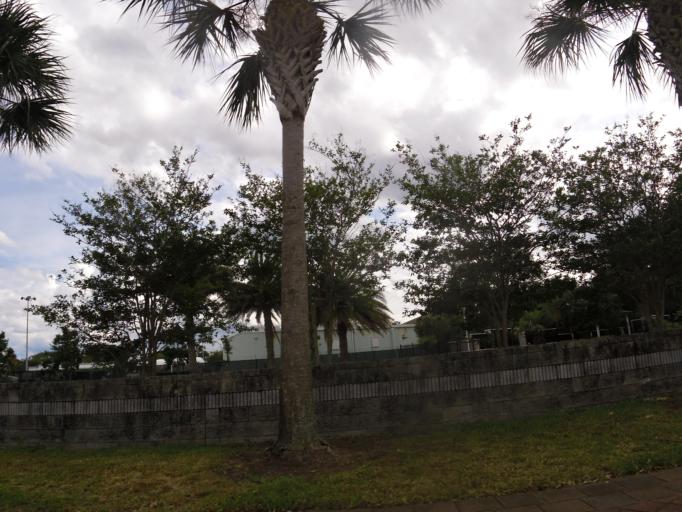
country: US
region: Florida
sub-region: Duval County
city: Jacksonville Beach
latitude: 30.2874
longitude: -81.4050
